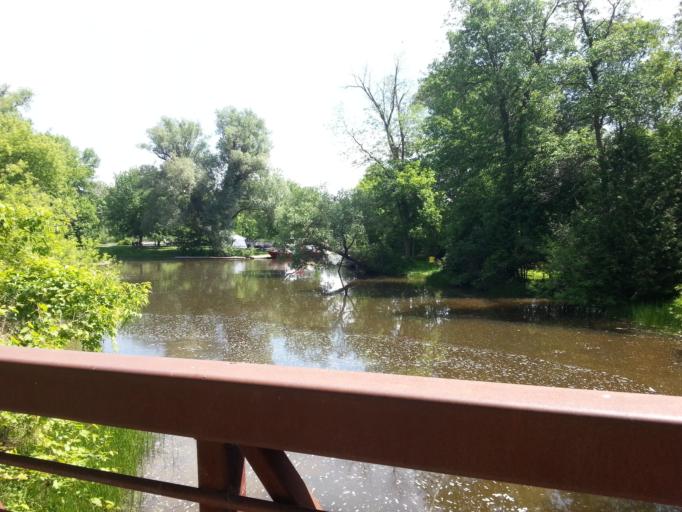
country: CA
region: Ontario
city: Ottawa
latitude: 45.3204
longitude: -75.6991
